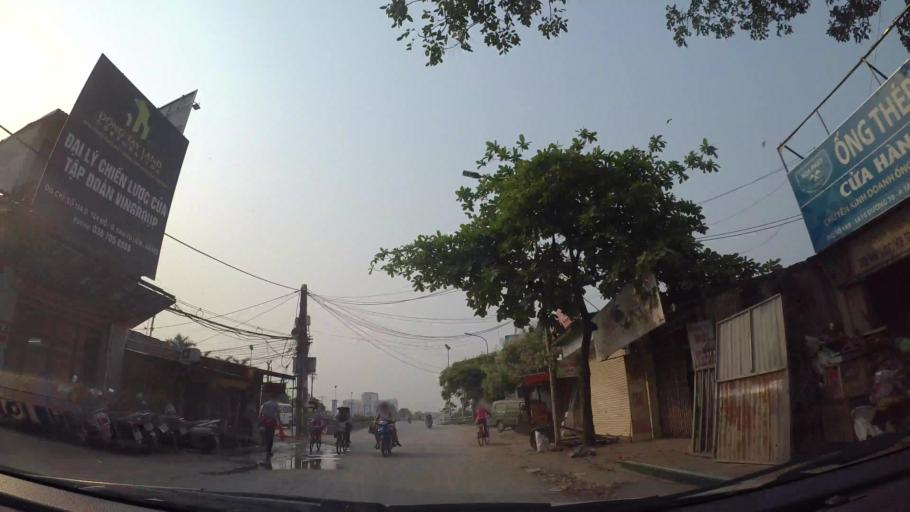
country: VN
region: Ha Noi
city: Cau Dien
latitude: 21.0053
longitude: 105.7493
